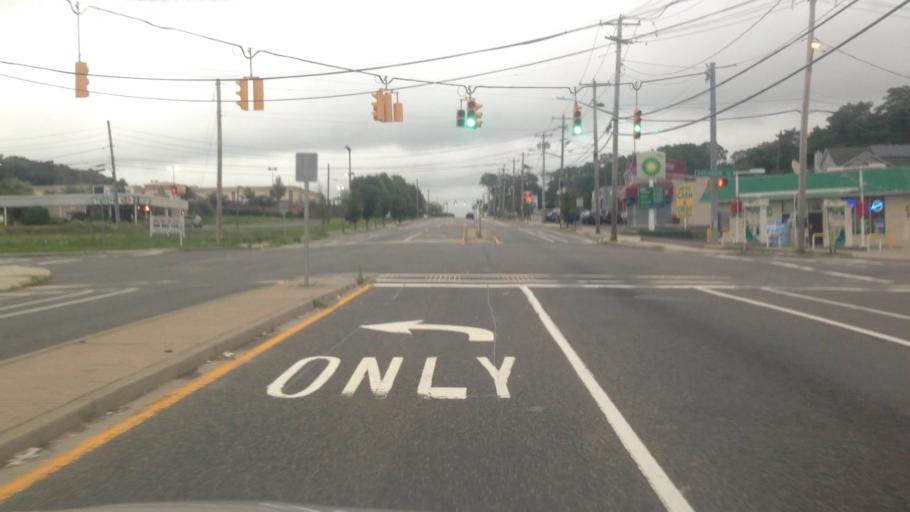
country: US
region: New York
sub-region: Suffolk County
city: Ronkonkoma
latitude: 40.8284
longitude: -73.0983
